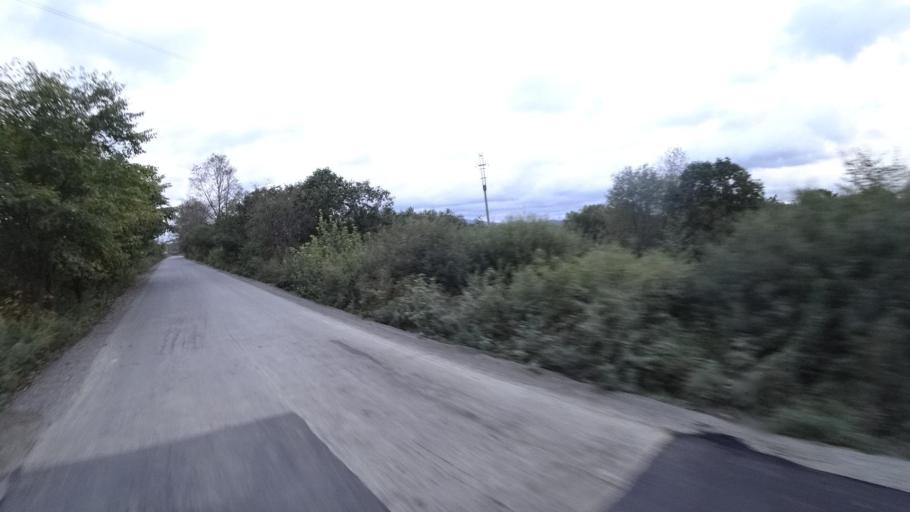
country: RU
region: Jewish Autonomous Oblast
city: Izvestkovyy
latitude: 48.9920
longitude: 131.5423
